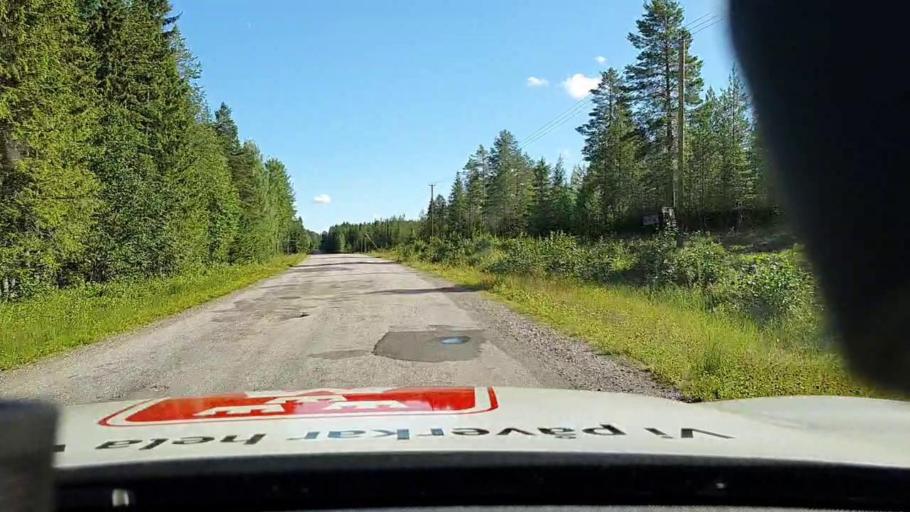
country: SE
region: Norrbotten
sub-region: Overkalix Kommun
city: OEverkalix
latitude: 66.2434
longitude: 23.0027
